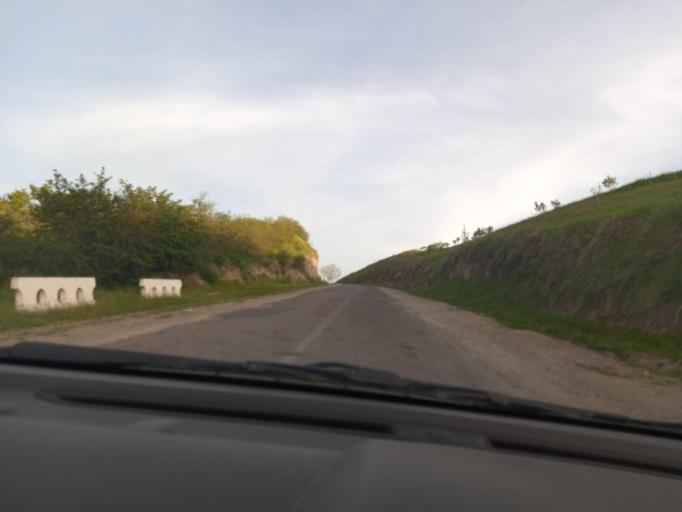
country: UZ
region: Toshkent
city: Parkent
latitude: 41.2401
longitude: 69.7329
